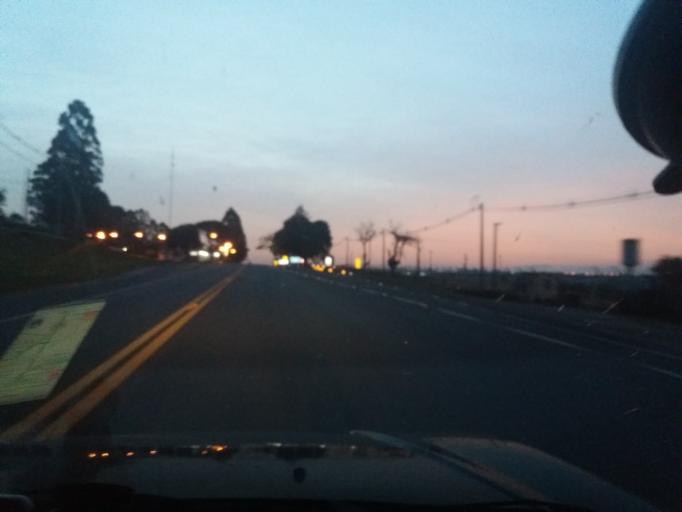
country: BR
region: Sao Paulo
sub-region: Itapeva
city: Itapeva
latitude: -23.9743
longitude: -48.8578
